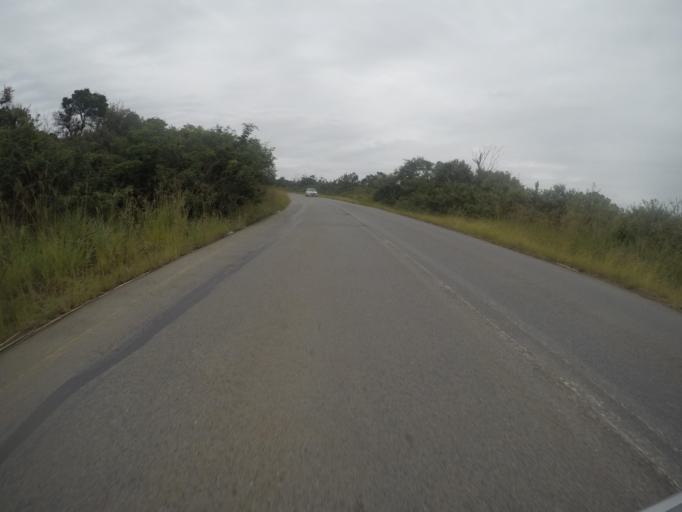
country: ZA
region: Eastern Cape
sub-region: Buffalo City Metropolitan Municipality
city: East London
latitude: -32.9425
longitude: 27.9304
